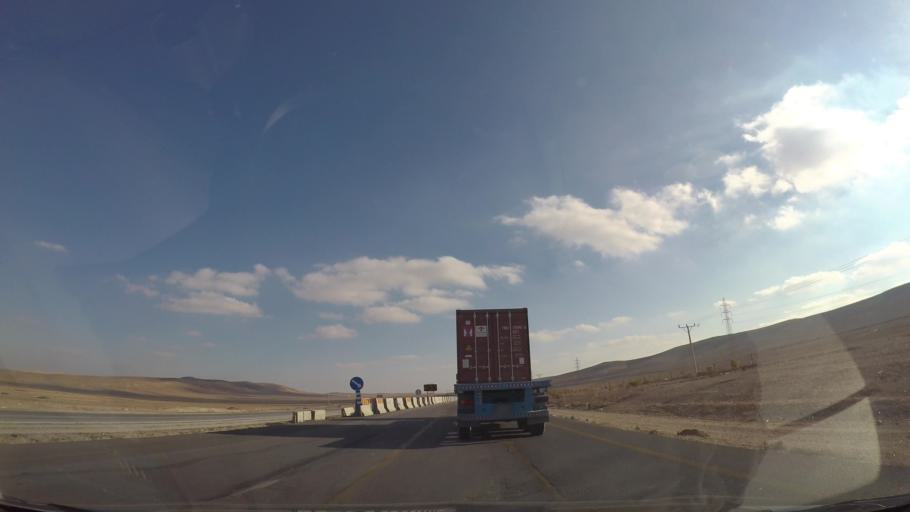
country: JO
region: Karak
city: Adir
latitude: 31.1932
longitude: 36.0171
